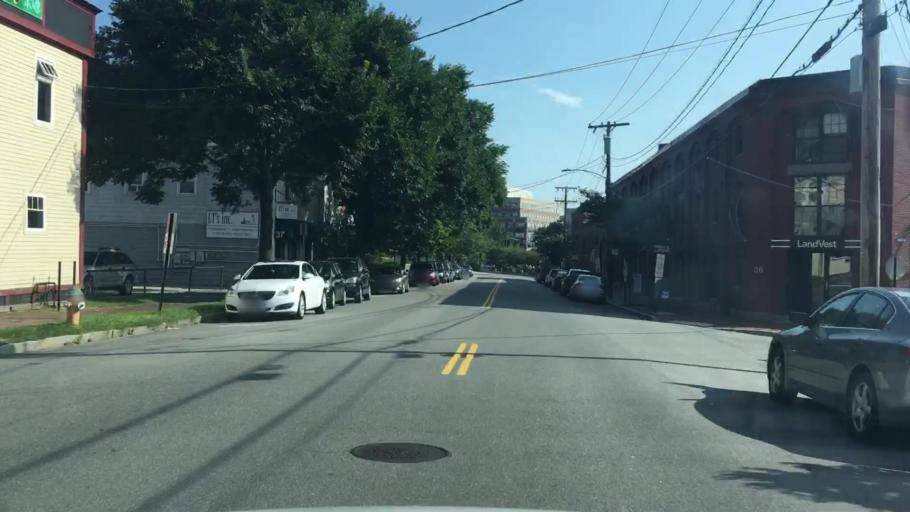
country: US
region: Maine
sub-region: Cumberland County
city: Portland
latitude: 43.6531
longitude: -70.2585
